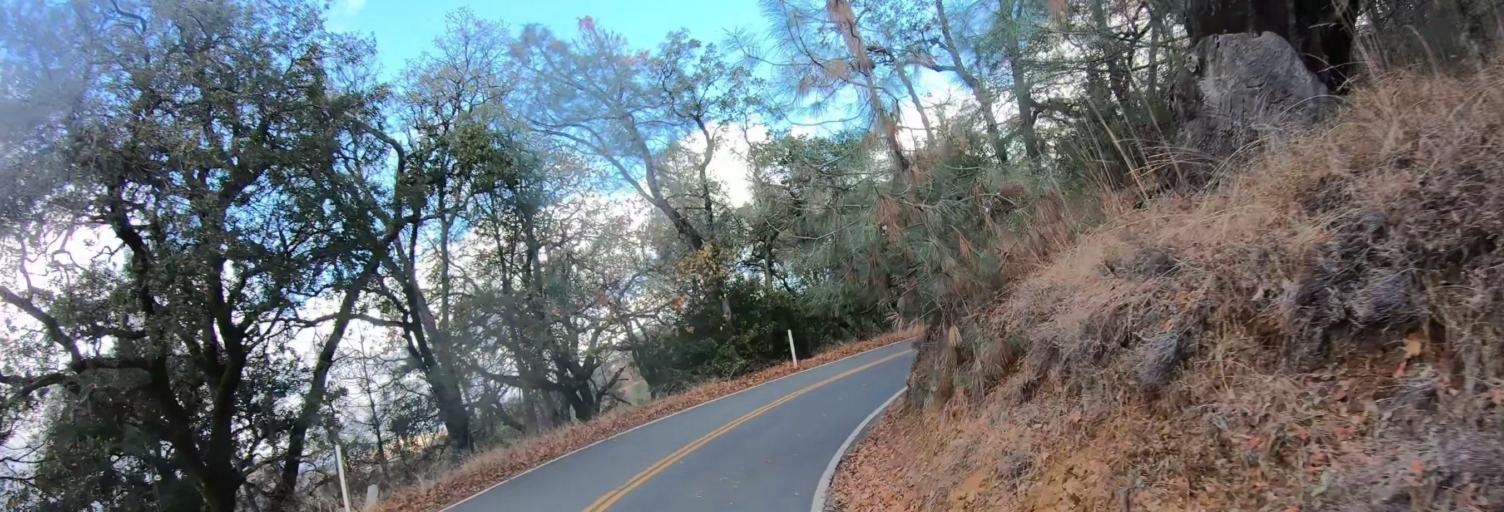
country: US
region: California
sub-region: Santa Clara County
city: East Foothills
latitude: 37.3333
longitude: -121.6673
